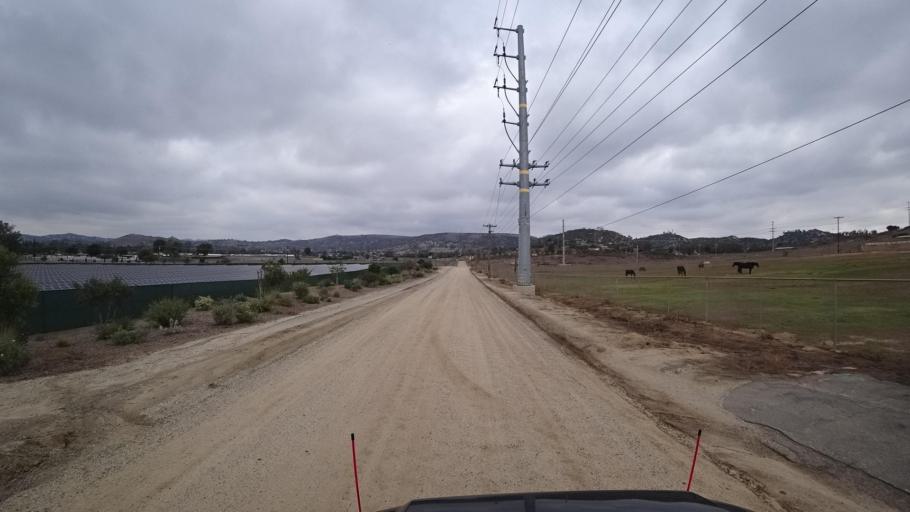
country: US
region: California
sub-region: San Diego County
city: Ramona
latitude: 33.0184
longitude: -116.8601
